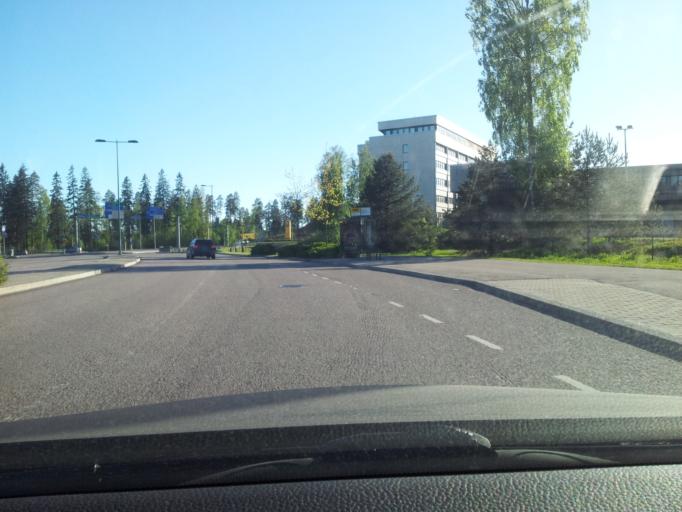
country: FI
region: Uusimaa
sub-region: Helsinki
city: Kauniainen
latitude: 60.2087
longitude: 24.7532
